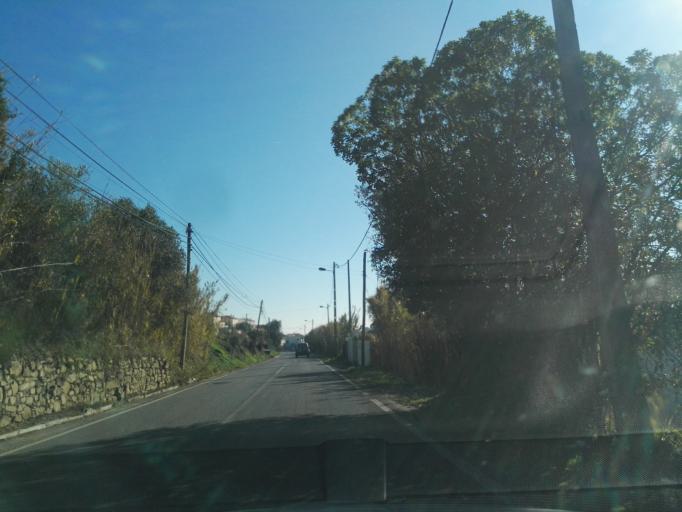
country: PT
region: Lisbon
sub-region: Vila Franca de Xira
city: Sao Joao dos Montes
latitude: 38.9391
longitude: -9.0277
